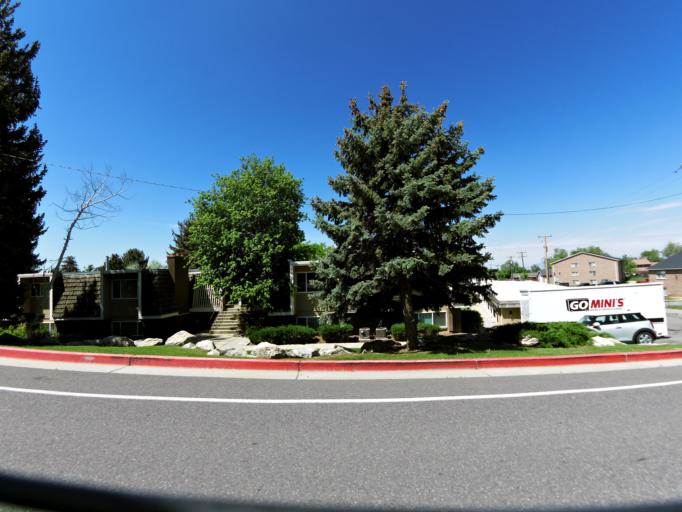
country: US
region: Utah
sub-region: Weber County
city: Washington Terrace
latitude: 41.1741
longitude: -111.9464
